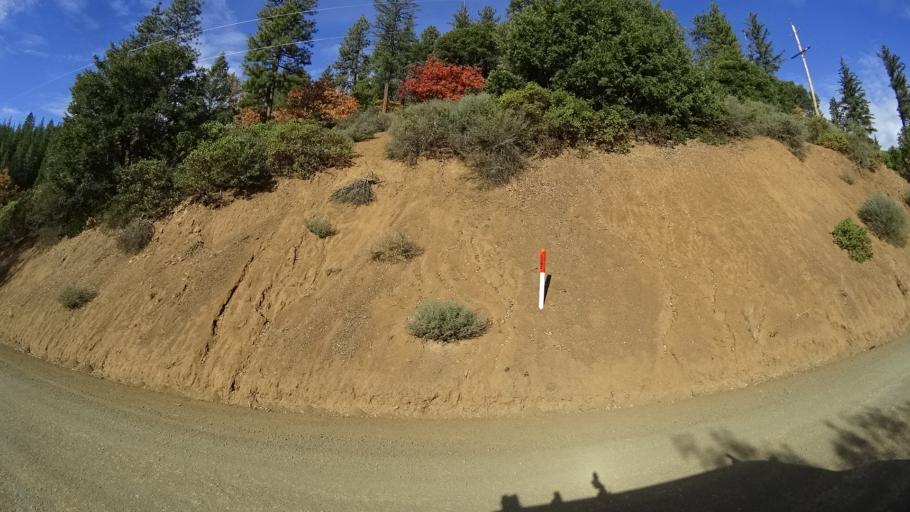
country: US
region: California
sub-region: Siskiyou County
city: Yreka
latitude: 41.7053
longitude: -122.8158
